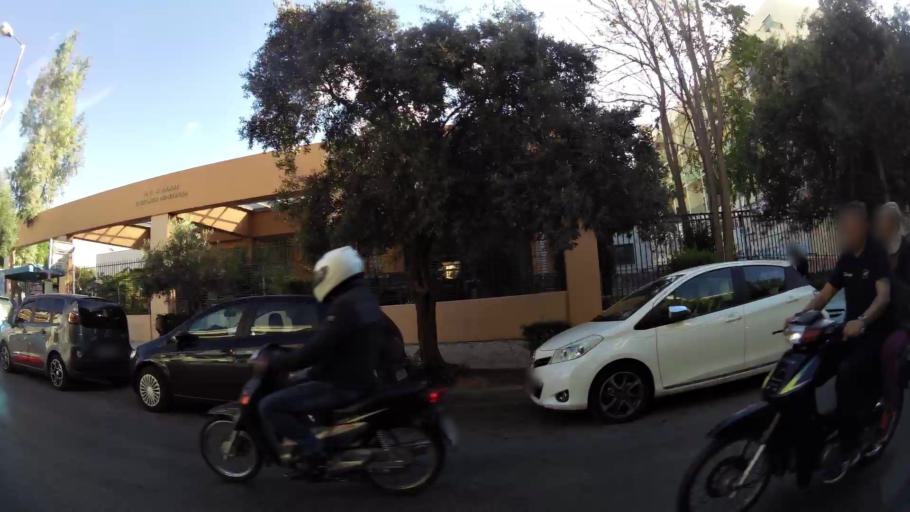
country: GR
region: Attica
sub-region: Nomos Piraios
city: Agios Ioannis Rentis
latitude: 37.9720
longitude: 23.6613
